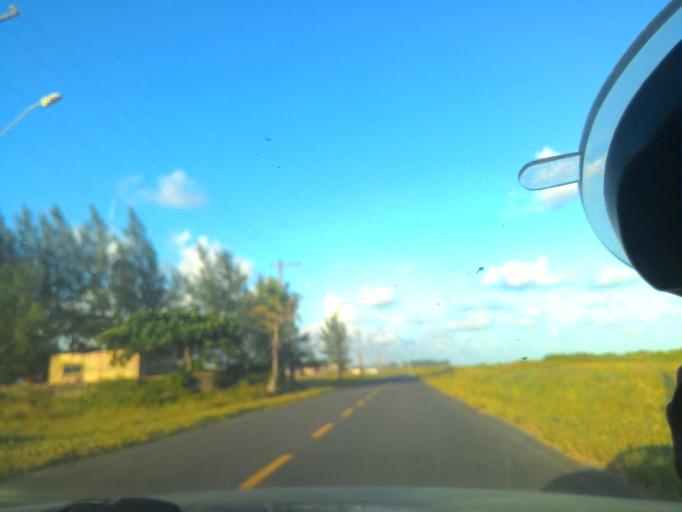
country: BR
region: Sao Paulo
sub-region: Iguape
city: Iguape
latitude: -24.8078
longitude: -47.6387
